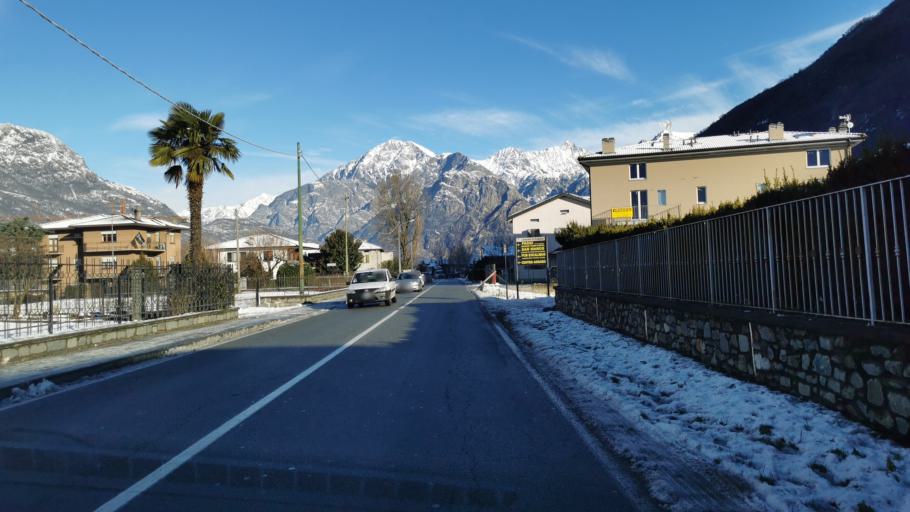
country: IT
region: Lombardy
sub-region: Provincia di Sondrio
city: Dubino
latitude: 46.1615
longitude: 9.4307
